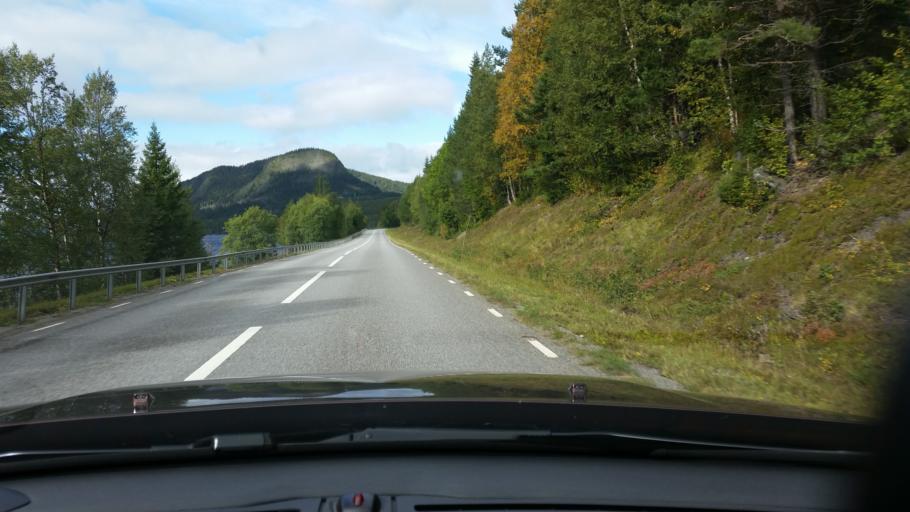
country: SE
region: Jaemtland
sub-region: Stroemsunds Kommun
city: Stroemsund
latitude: 64.3711
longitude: 14.6558
